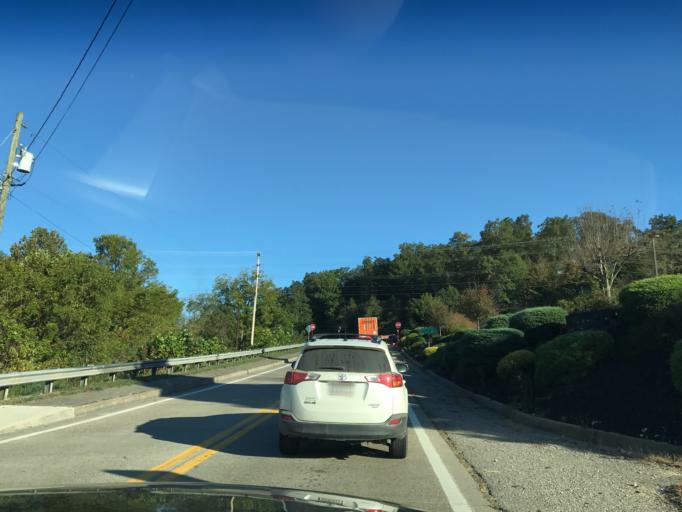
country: US
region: West Virginia
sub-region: Ritchie County
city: Harrisville
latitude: 39.2658
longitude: -81.0567
